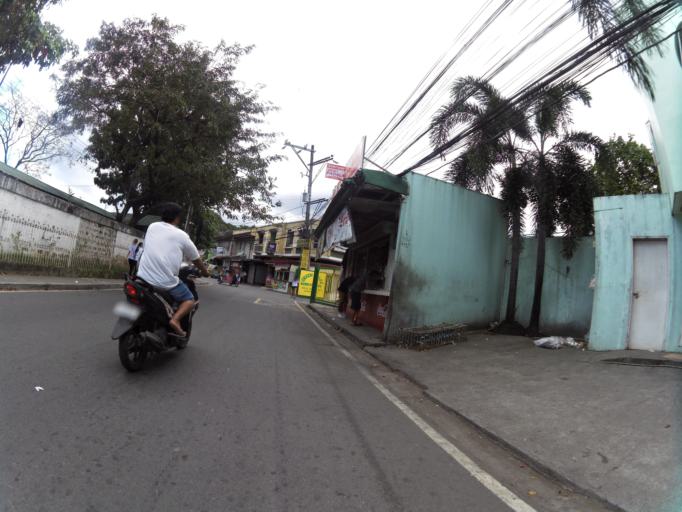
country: PH
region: Calabarzon
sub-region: Province of Rizal
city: Antipolo
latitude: 14.6328
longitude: 121.1085
